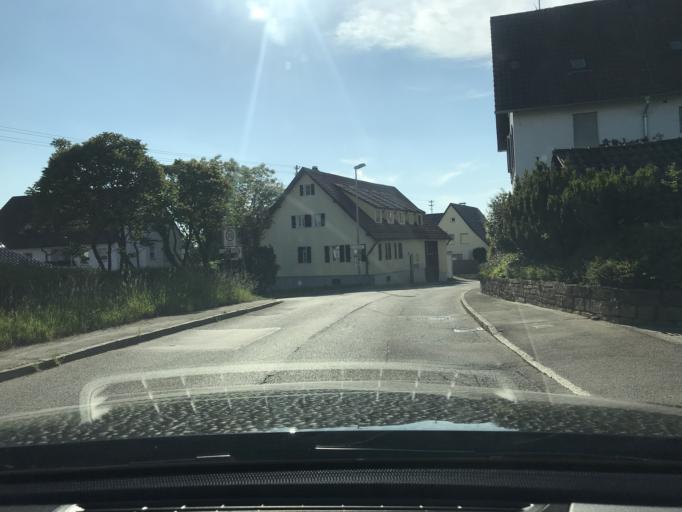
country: DE
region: Baden-Wuerttemberg
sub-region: Regierungsbezirk Stuttgart
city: Schwaikheim
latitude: 48.8906
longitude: 9.3207
